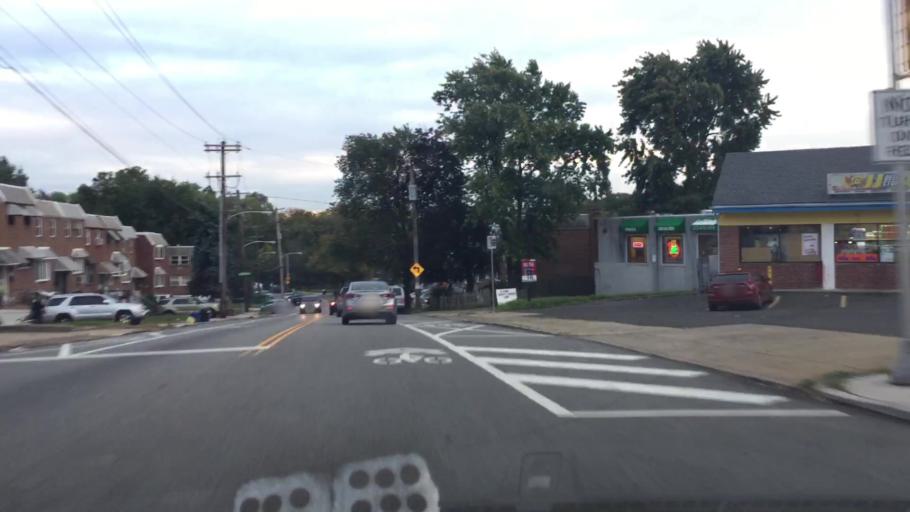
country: US
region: New Jersey
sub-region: Burlington County
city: Riverton
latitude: 40.0630
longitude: -75.0220
